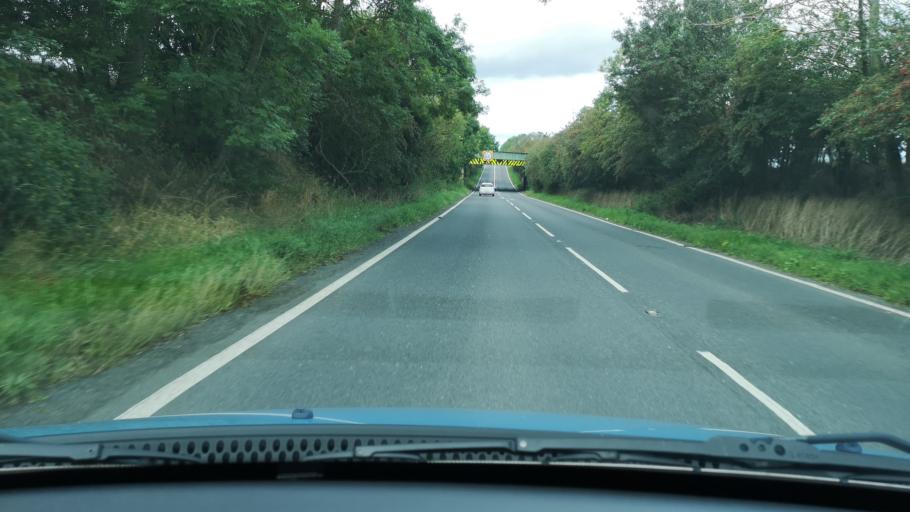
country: GB
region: England
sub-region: City and Borough of Wakefield
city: Badsworth
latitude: 53.6292
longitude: -1.3188
